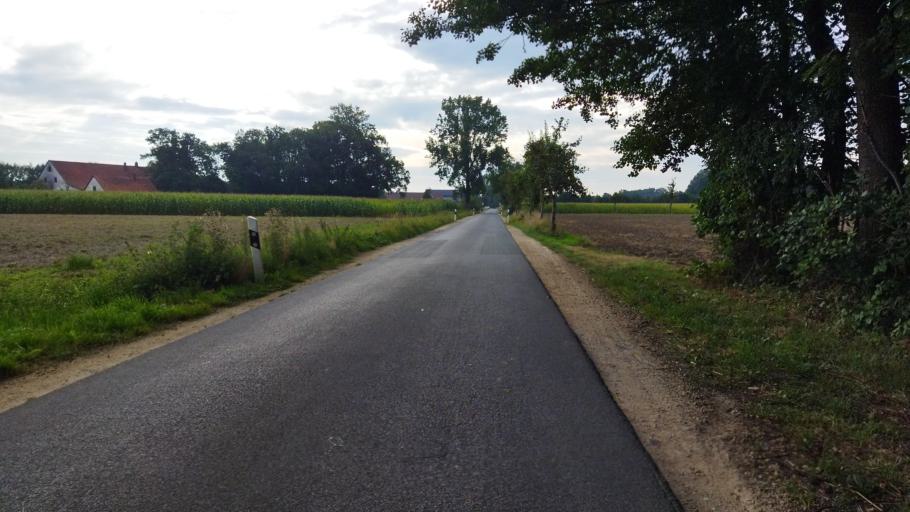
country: DE
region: Lower Saxony
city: Bad Laer
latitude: 52.0885
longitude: 8.1046
